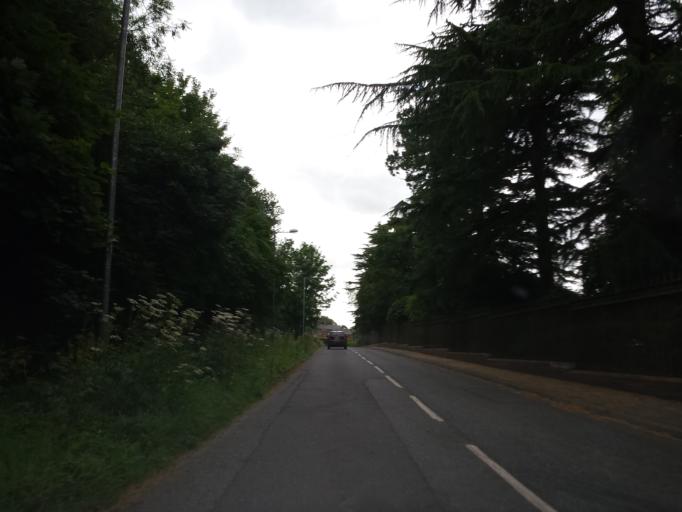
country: GB
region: Scotland
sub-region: Dumfries and Galloway
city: Dumfries
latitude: 55.0543
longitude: -3.5947
